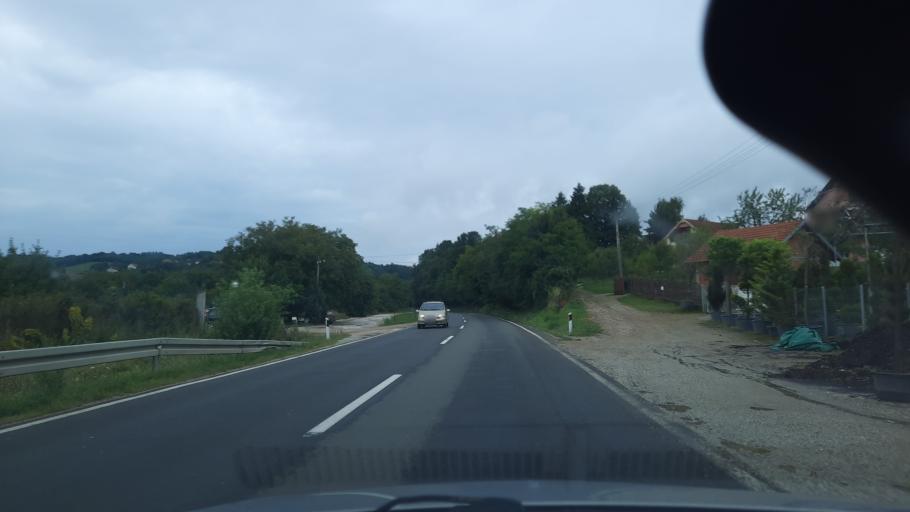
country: RS
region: Central Serbia
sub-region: Sumadijski Okrug
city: Knic
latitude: 43.9683
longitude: 20.8104
